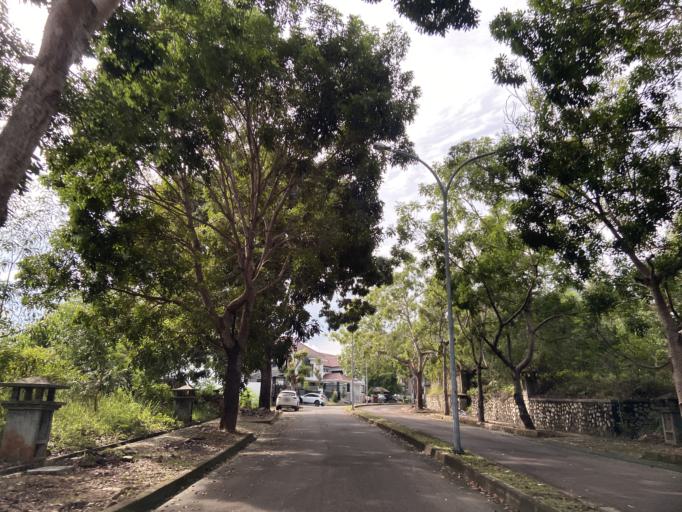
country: SG
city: Singapore
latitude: 1.0998
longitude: 104.0280
